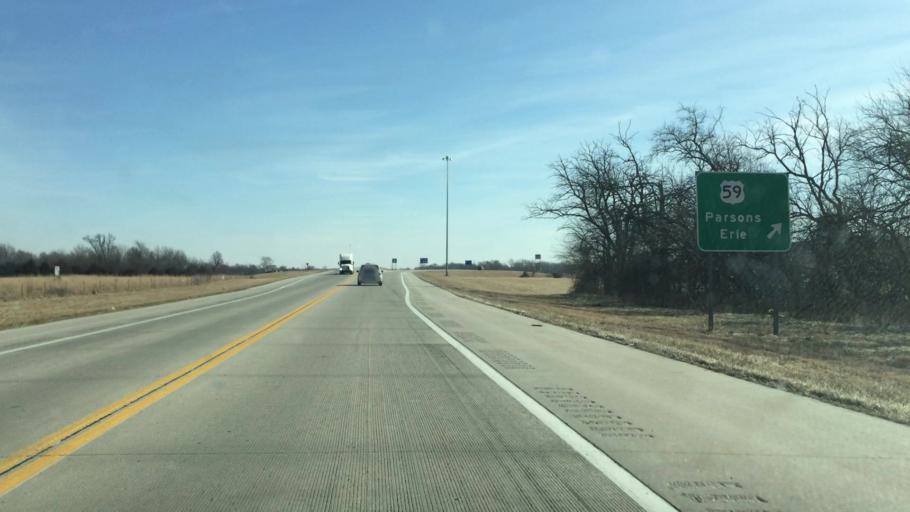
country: US
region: Kansas
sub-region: Labette County
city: Parsons
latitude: 37.3678
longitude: -95.2659
